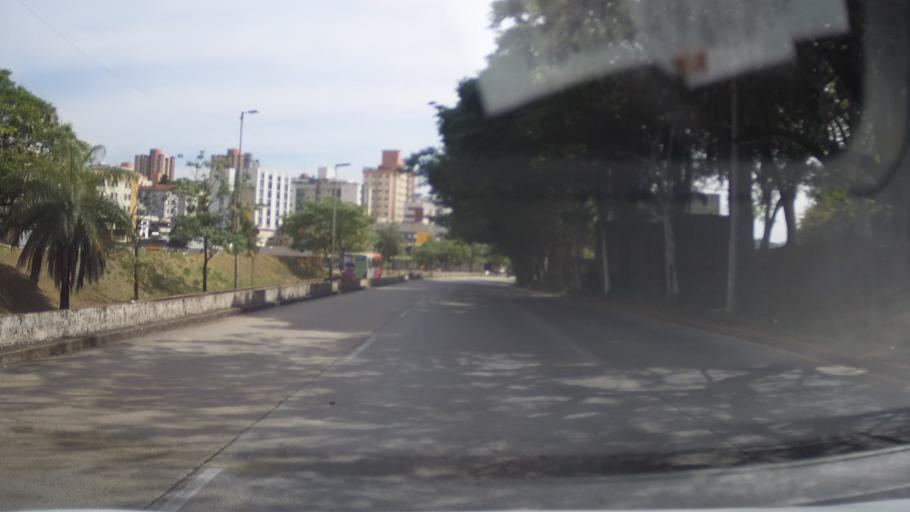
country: BR
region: Minas Gerais
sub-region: Belo Horizonte
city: Belo Horizonte
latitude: -19.9296
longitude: -43.9913
